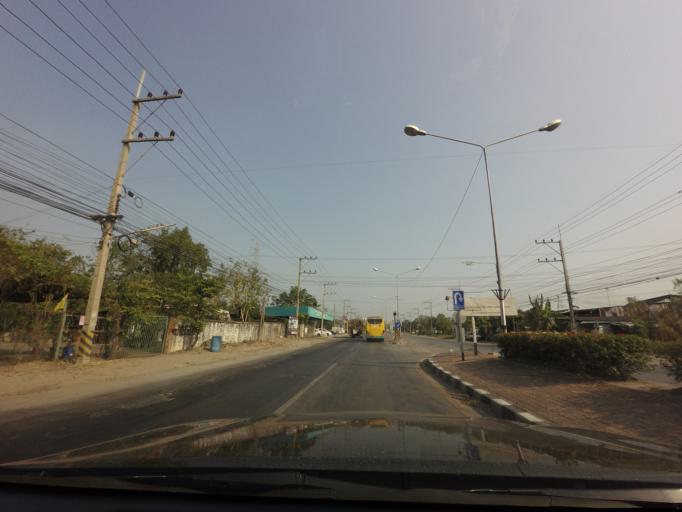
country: TH
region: Kanchanaburi
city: Tha Maka
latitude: 13.8820
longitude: 99.8047
